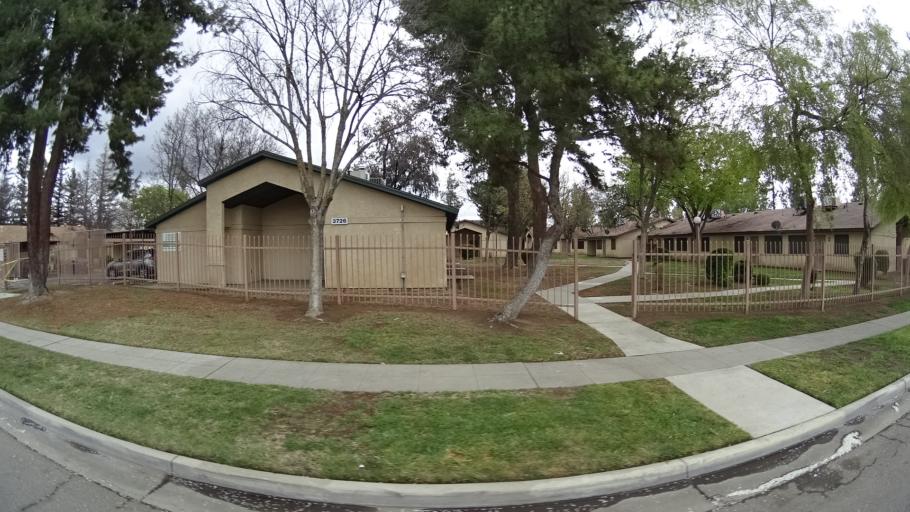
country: US
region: California
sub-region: Fresno County
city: West Park
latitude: 36.7851
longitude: -119.8399
